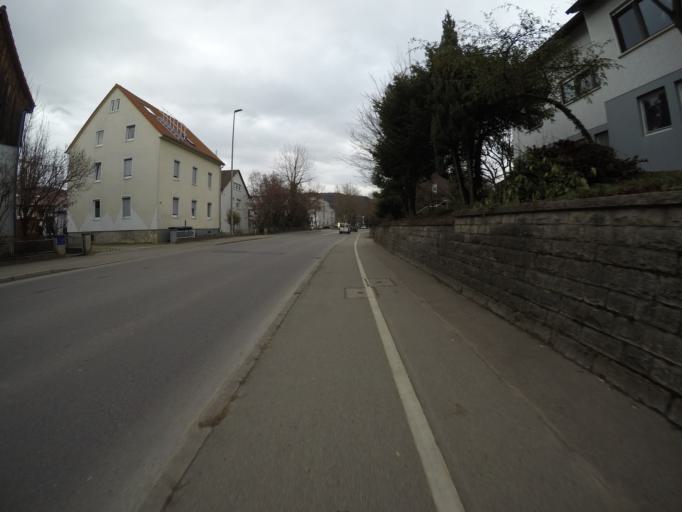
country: DE
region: Baden-Wuerttemberg
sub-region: Tuebingen Region
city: Pfullingen
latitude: 48.4700
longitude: 9.2210
